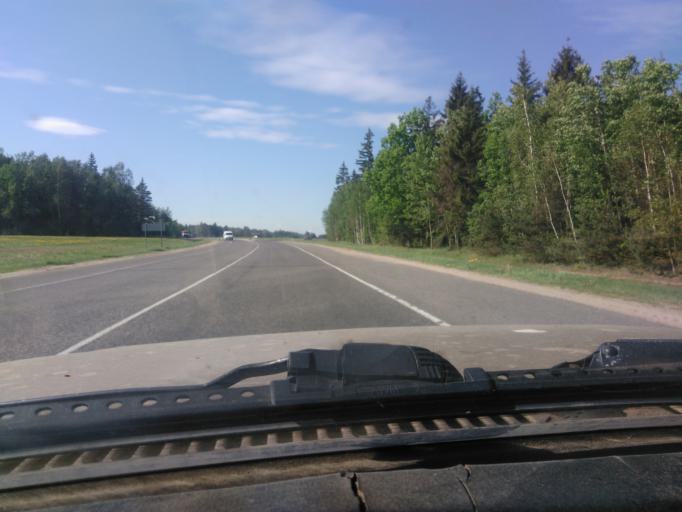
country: BY
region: Mogilev
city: Myazhysyatki
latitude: 53.8037
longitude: 30.2064
